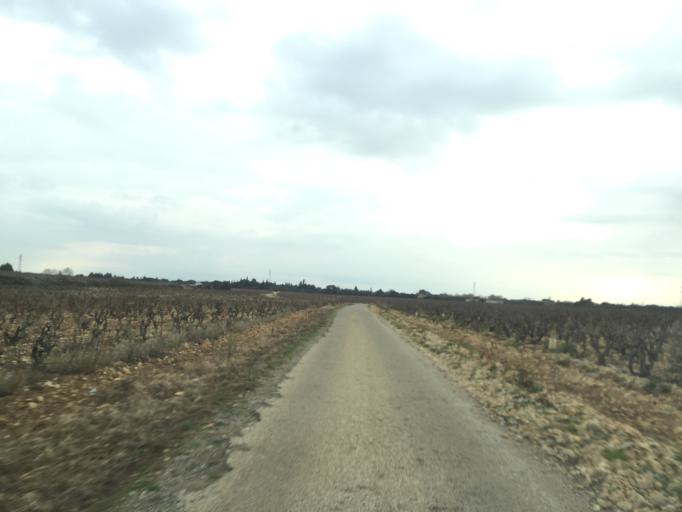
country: FR
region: Provence-Alpes-Cote d'Azur
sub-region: Departement du Vaucluse
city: Chateauneuf-du-Pape
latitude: 44.0335
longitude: 4.8518
